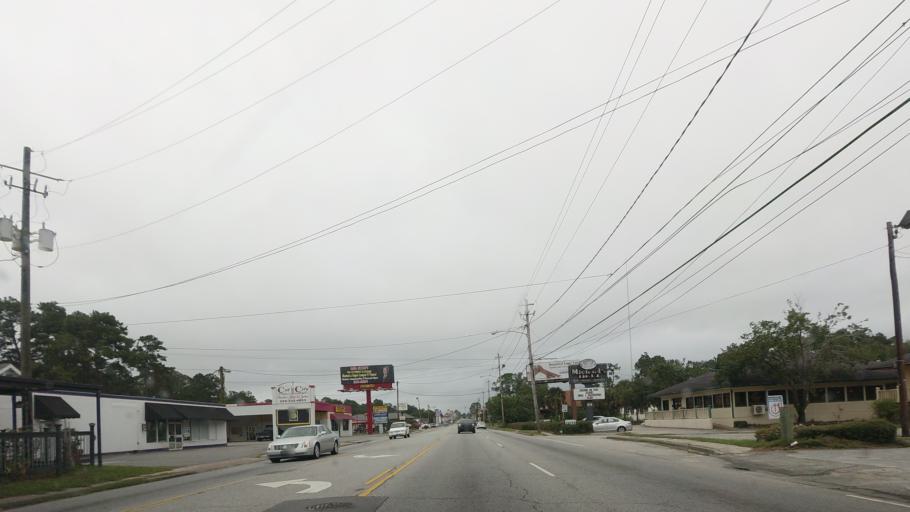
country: US
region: Georgia
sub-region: Lowndes County
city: Valdosta
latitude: 30.8466
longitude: -83.2804
